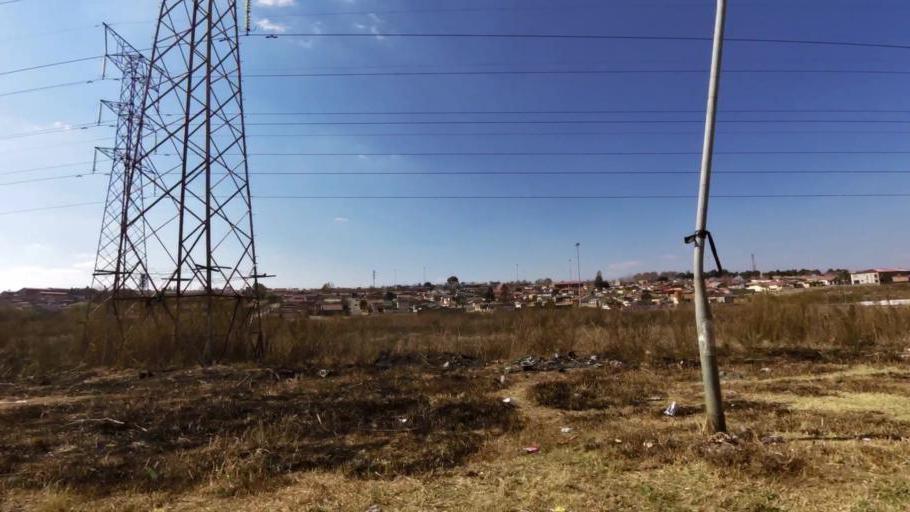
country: ZA
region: Gauteng
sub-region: City of Johannesburg Metropolitan Municipality
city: Soweto
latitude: -26.2341
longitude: 27.8866
